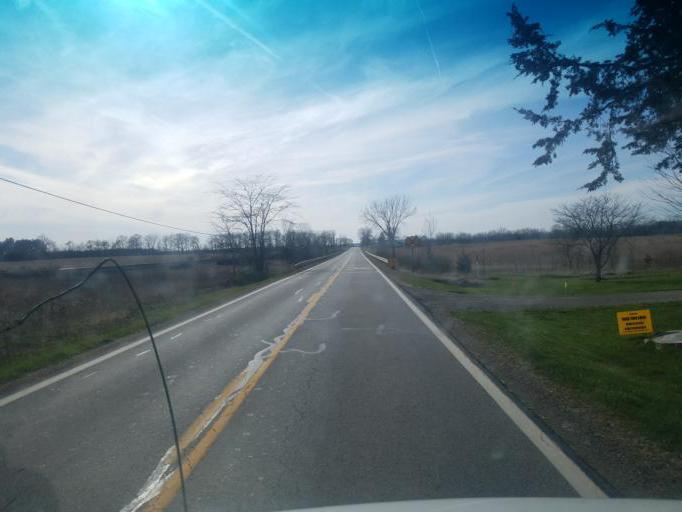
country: US
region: Ohio
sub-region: Champaign County
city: North Lewisburg
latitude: 40.3403
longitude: -83.4825
